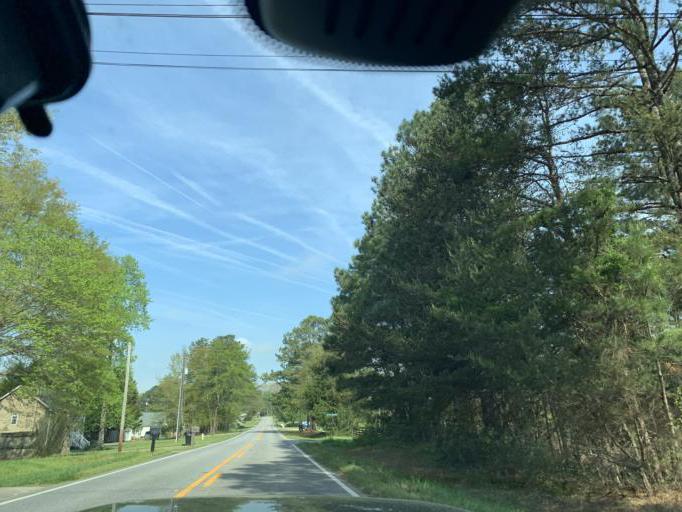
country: US
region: Georgia
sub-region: Forsyth County
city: Cumming
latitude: 34.2144
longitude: -84.0776
